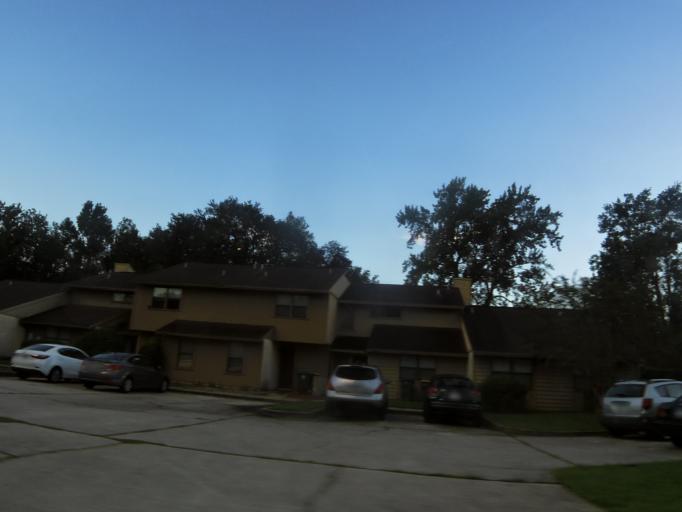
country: US
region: Florida
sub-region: Duval County
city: Jacksonville
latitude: 30.2319
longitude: -81.6035
